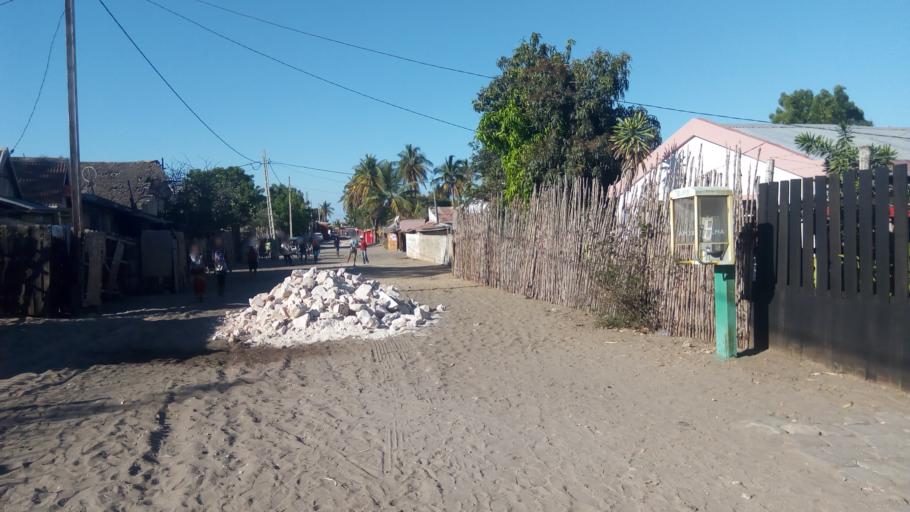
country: MG
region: Menabe
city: Morondava
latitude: -20.2979
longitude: 44.2801
